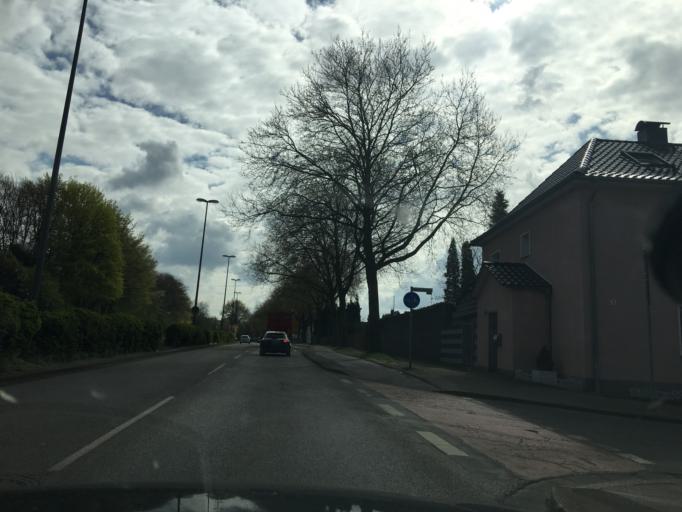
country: DE
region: North Rhine-Westphalia
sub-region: Regierungsbezirk Munster
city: Gladbeck
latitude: 51.5734
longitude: 7.0509
